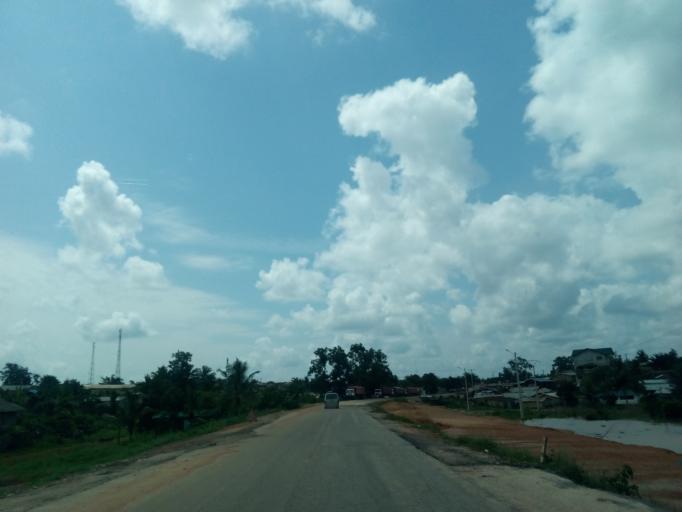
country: CI
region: Sud-Comoe
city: Mafere
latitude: 5.2873
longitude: -2.7955
